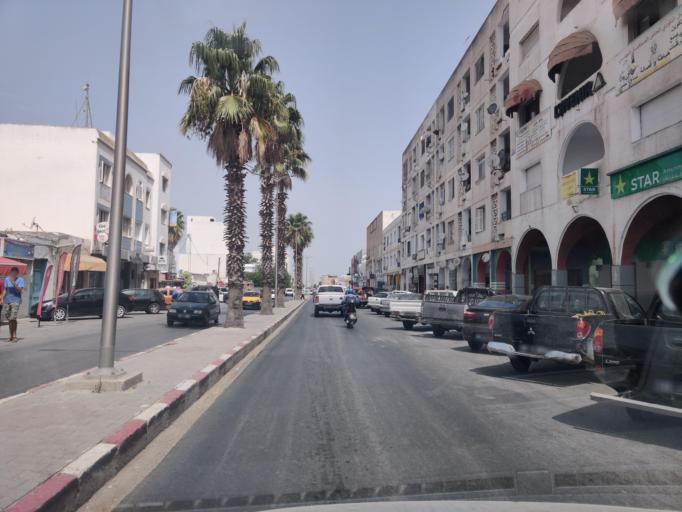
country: TN
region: Nabul
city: Bu `Urqub
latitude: 36.5996
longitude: 10.4982
